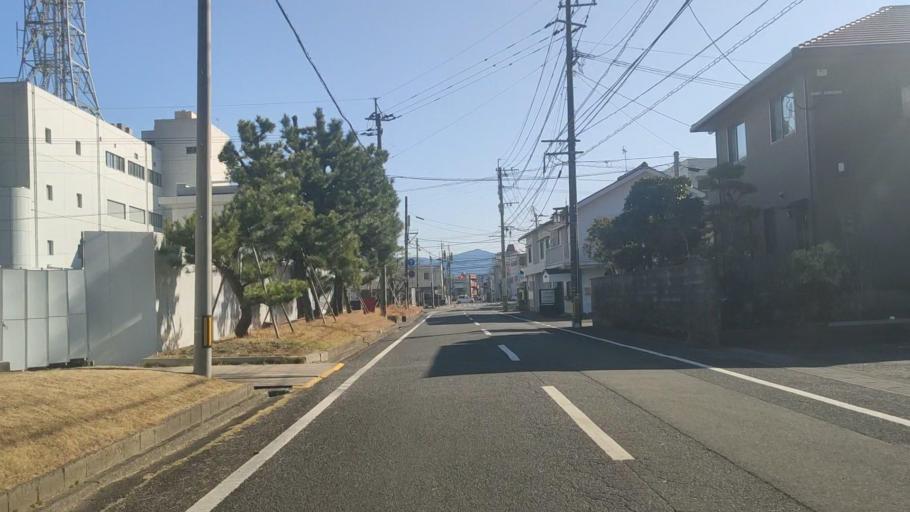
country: JP
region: Oita
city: Saiki
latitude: 32.9607
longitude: 131.8960
